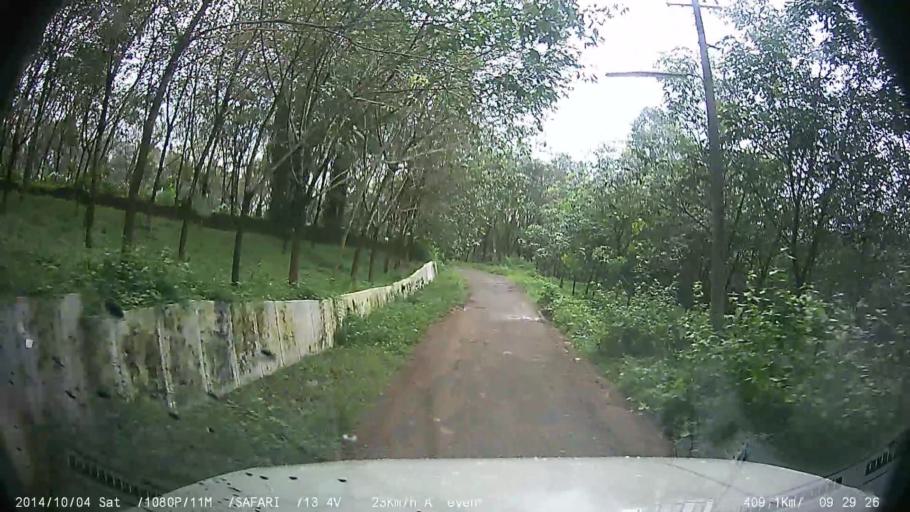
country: IN
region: Kerala
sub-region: Kottayam
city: Palackattumala
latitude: 9.7855
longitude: 76.5742
